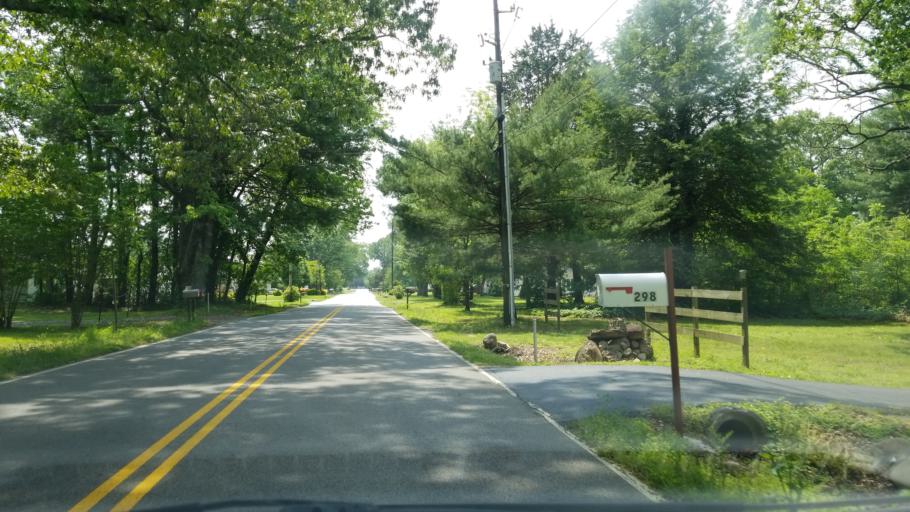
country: US
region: Tennessee
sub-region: Hamilton County
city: Falling Water
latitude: 35.2312
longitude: -85.2291
